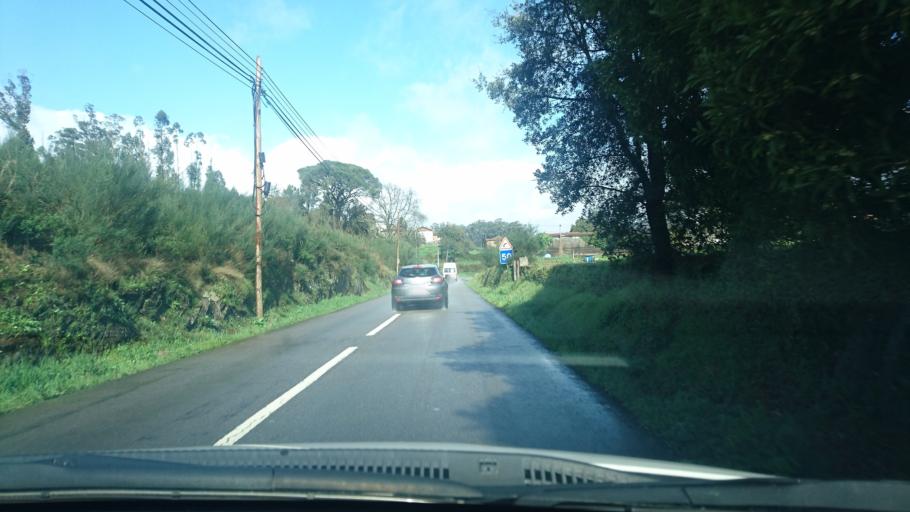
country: PT
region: Porto
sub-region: Paredes
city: Recarei
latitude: 41.1470
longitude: -8.4168
